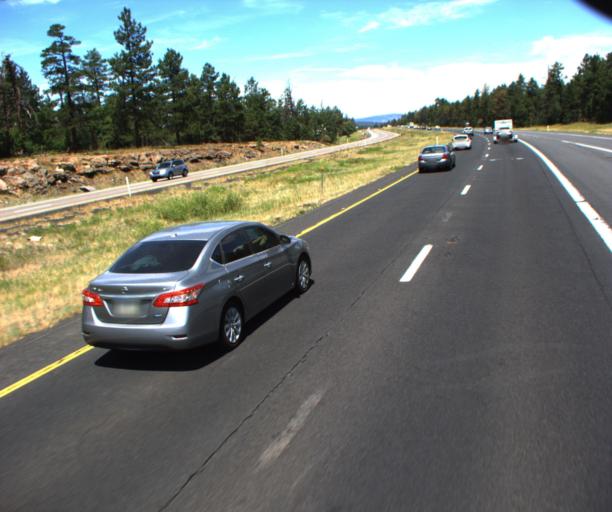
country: US
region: Arizona
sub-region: Coconino County
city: Sedona
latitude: 34.8561
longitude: -111.6089
